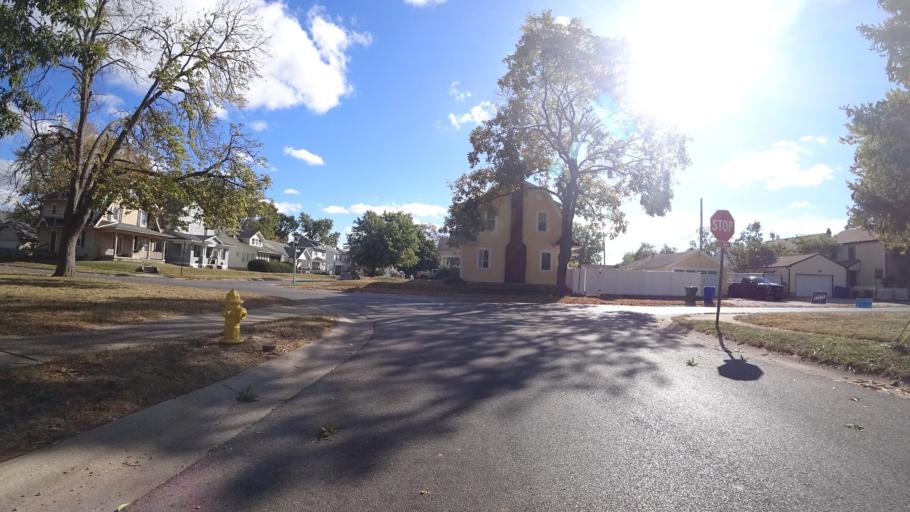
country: US
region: Ohio
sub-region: Butler County
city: Fairfield
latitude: 39.3660
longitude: -84.5529
